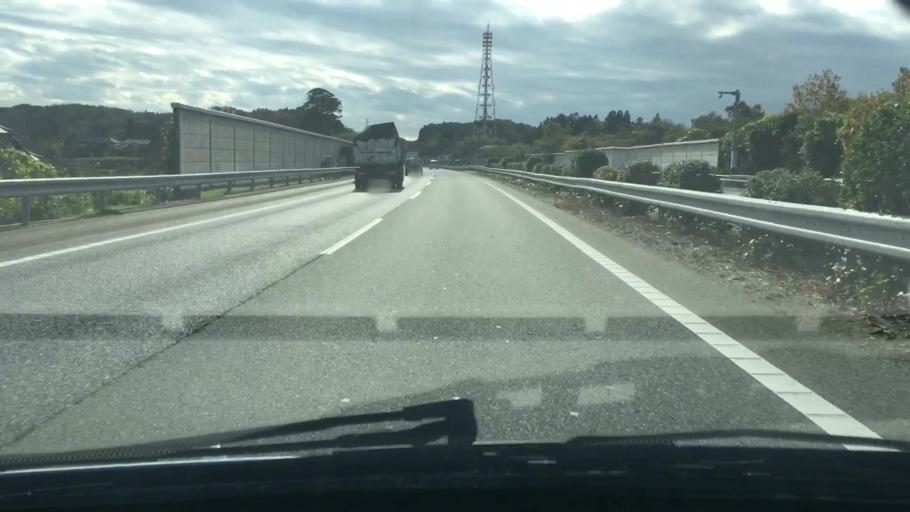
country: JP
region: Chiba
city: Ichihara
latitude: 35.4759
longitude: 140.0817
